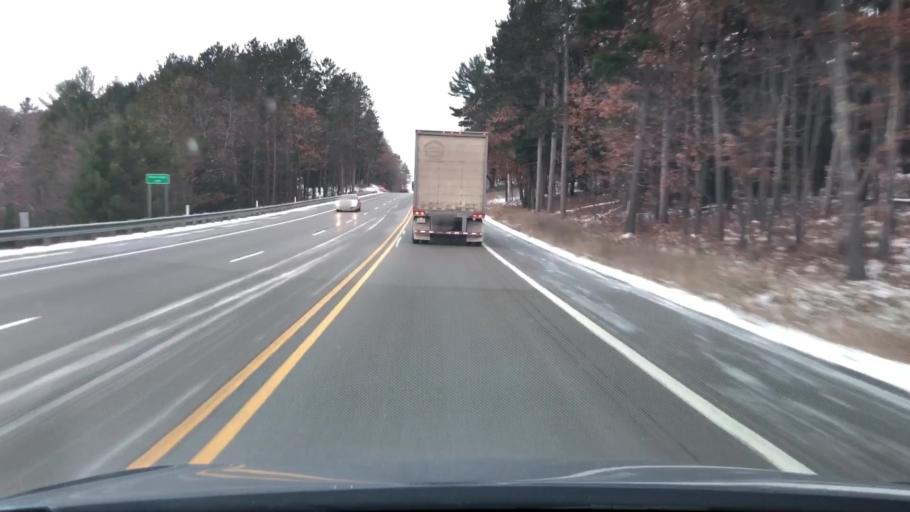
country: US
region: Michigan
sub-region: Wexford County
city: Cadillac
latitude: 44.1852
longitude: -85.3869
